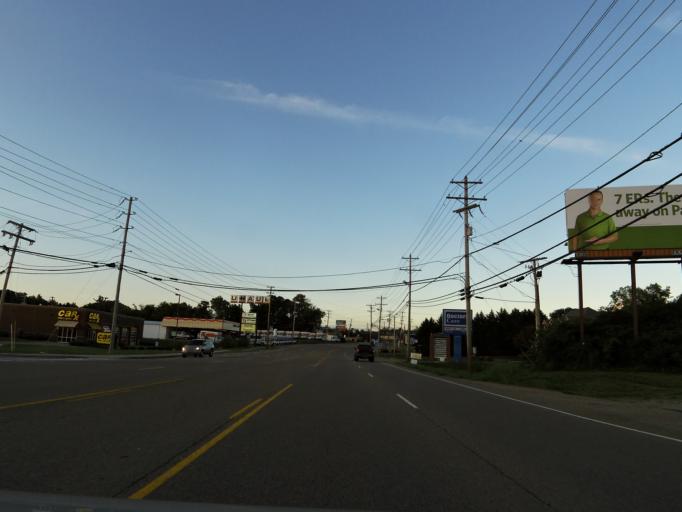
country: US
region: Tennessee
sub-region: Knox County
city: Farragut
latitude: 35.8921
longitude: -84.1450
